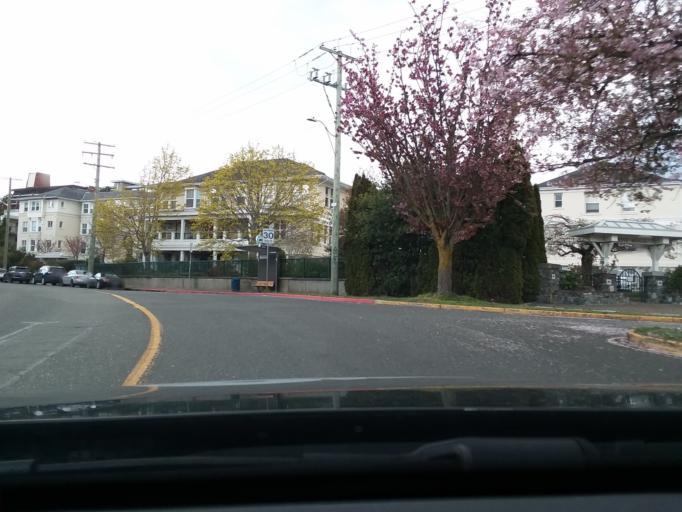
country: CA
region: British Columbia
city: Victoria
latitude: 48.4199
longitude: -123.3605
